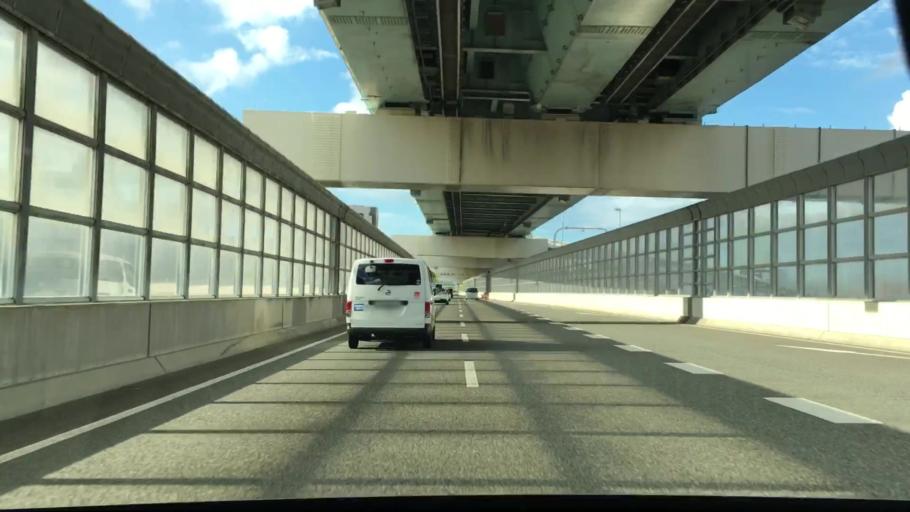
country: JP
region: Fukuoka
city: Fukuoka-shi
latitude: 33.5712
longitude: 130.3168
